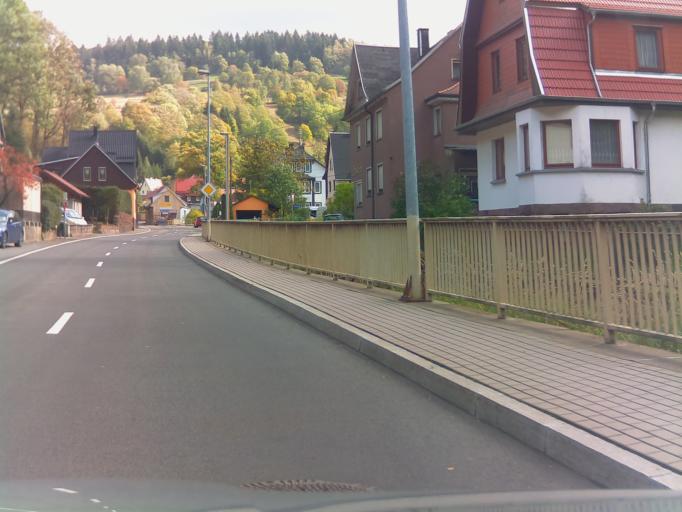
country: DE
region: Thuringia
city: Unterschonau
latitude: 50.7135
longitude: 10.5849
